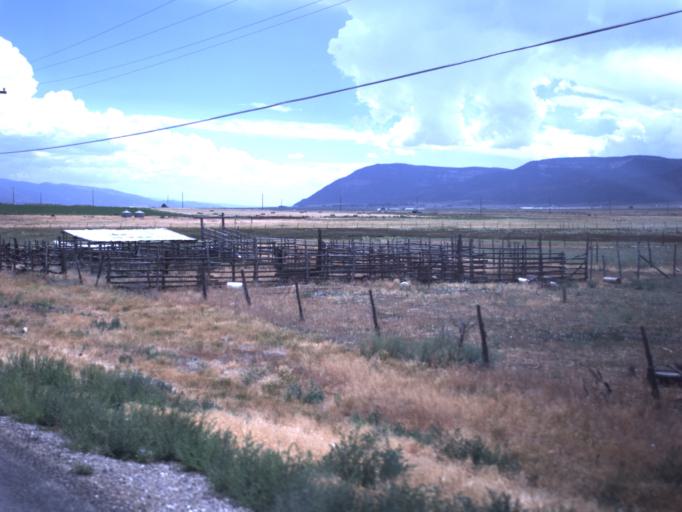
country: US
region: Utah
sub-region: Sanpete County
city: Moroni
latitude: 39.5592
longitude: -111.6015
